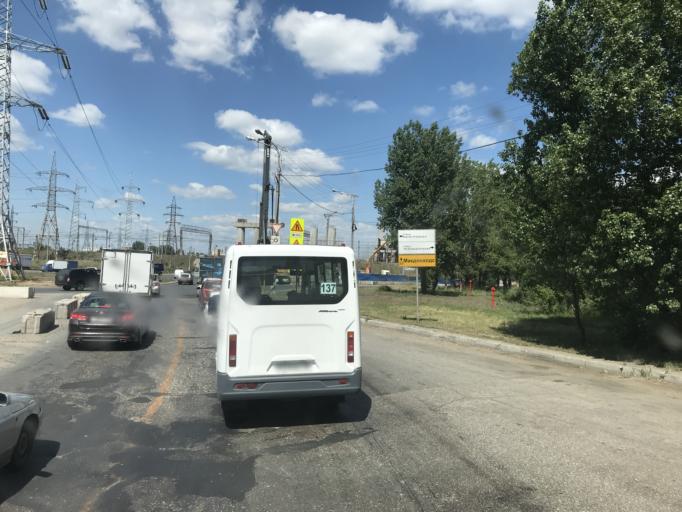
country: RU
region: Samara
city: Zhigulevsk
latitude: 53.4790
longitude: 49.5123
